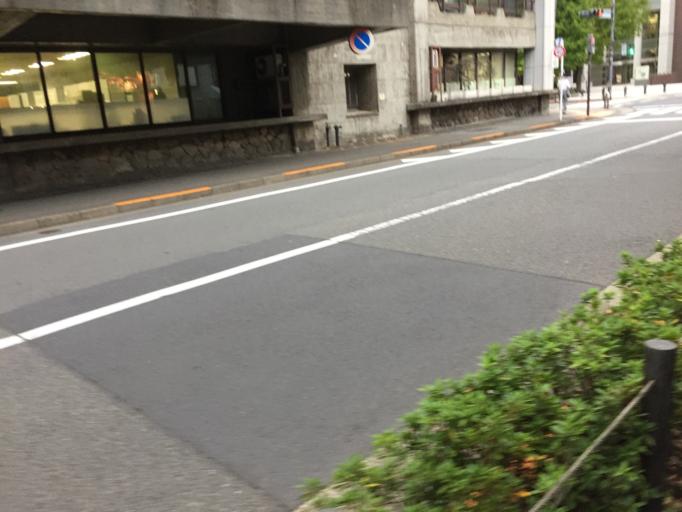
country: JP
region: Tokyo
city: Tokyo
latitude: 35.6465
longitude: 139.6536
